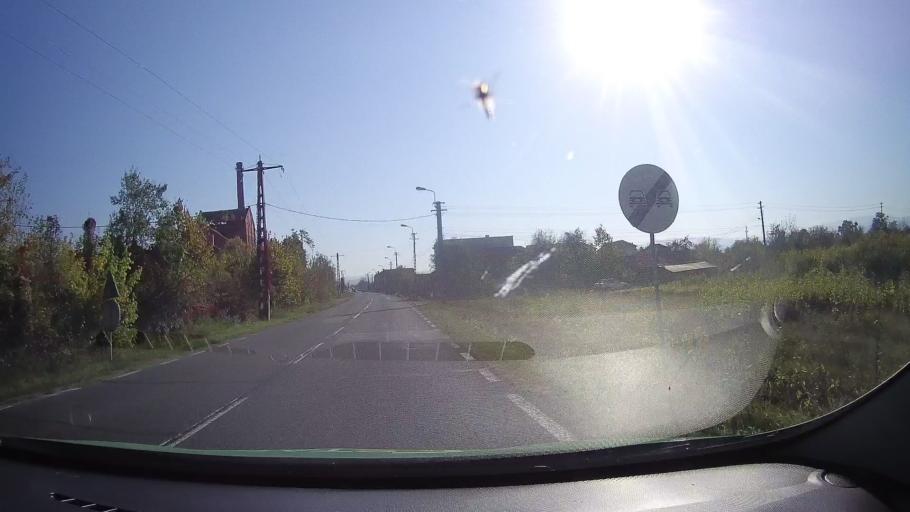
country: RO
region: Timis
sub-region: Comuna Margina
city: Margina
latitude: 45.8585
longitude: 22.2622
